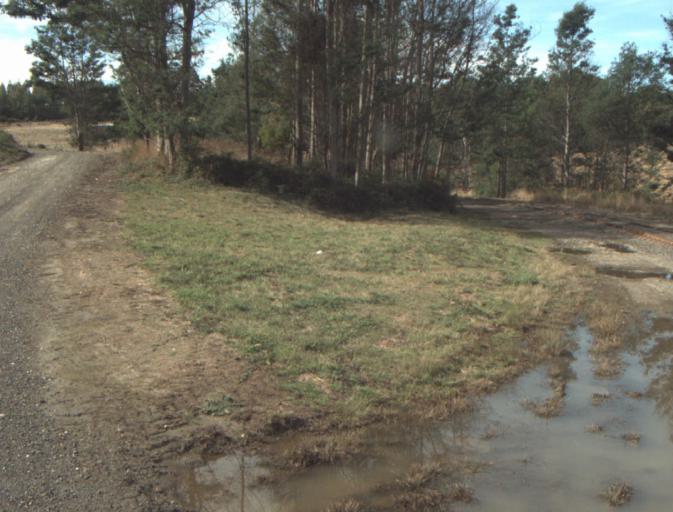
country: AU
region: Tasmania
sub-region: Launceston
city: Mayfield
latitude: -41.1967
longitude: 147.1945
